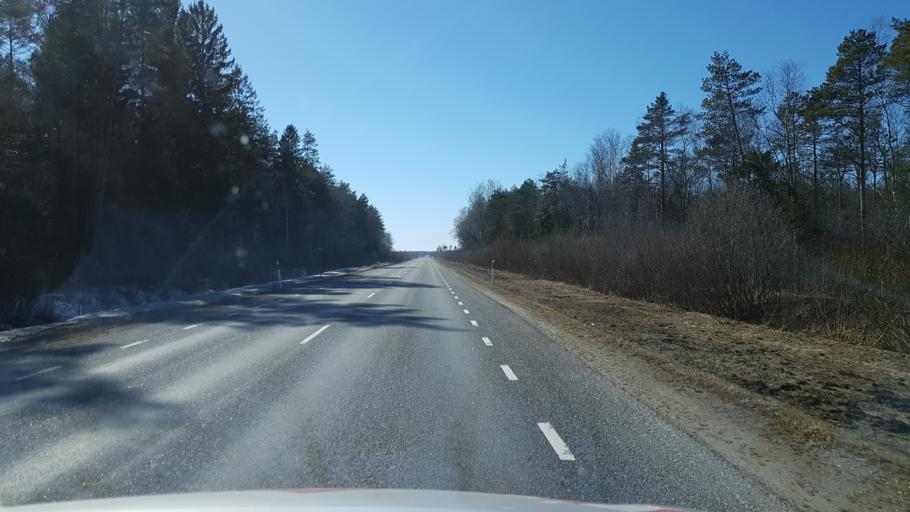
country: EE
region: Ida-Virumaa
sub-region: Aseri vald
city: Aseri
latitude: 59.3551
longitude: 26.7160
